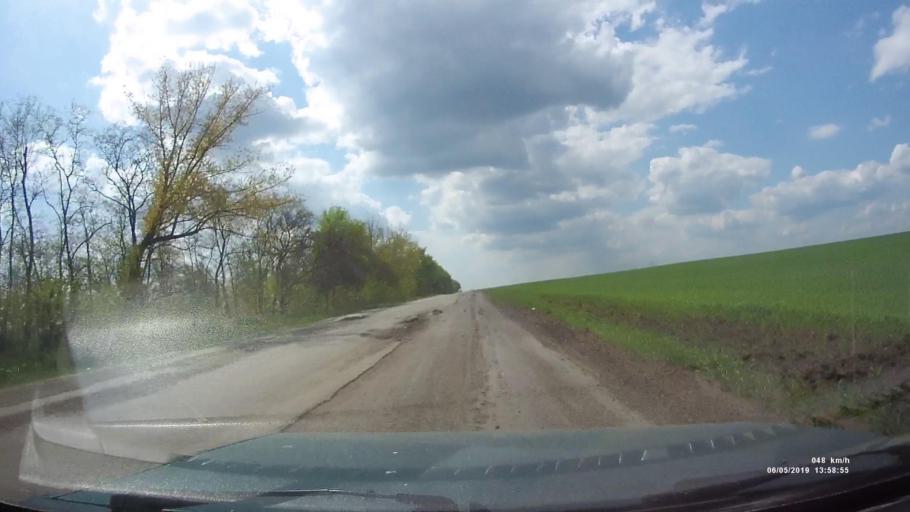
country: RU
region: Rostov
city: Shakhty
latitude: 47.6854
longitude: 40.4059
